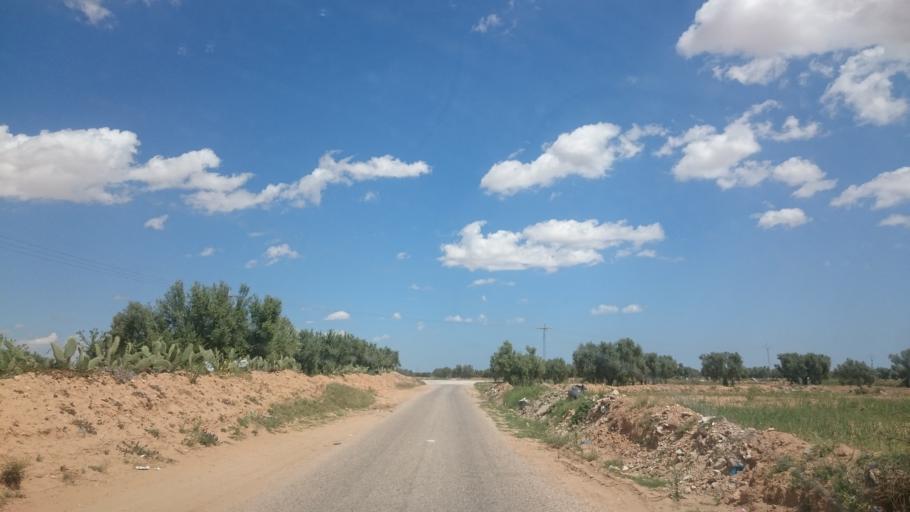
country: TN
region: Safaqis
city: Sfax
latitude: 34.6972
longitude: 10.5859
